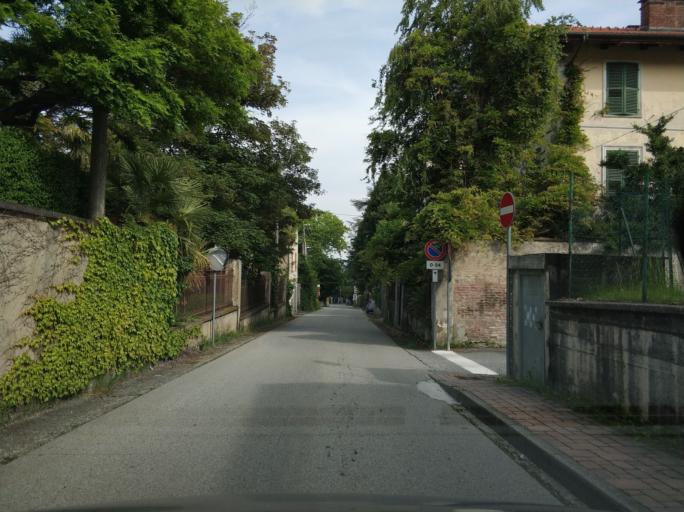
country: IT
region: Piedmont
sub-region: Provincia di Torino
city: Corio
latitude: 45.3113
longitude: 7.5340
